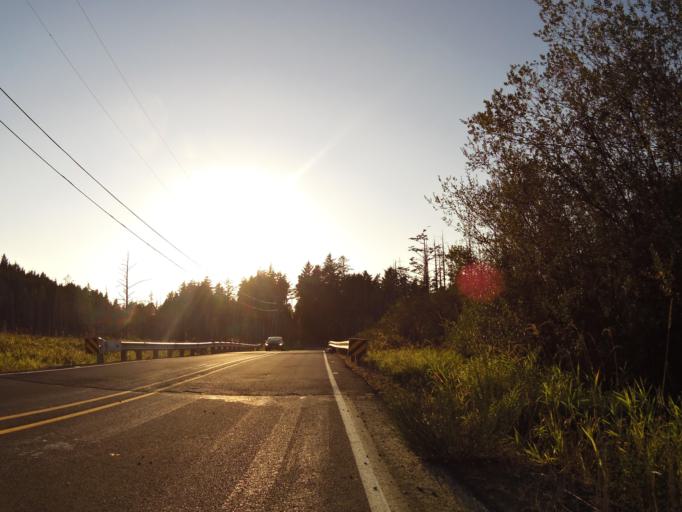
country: US
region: Oregon
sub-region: Lincoln County
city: Lincoln City
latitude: 44.9616
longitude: -124.0024
